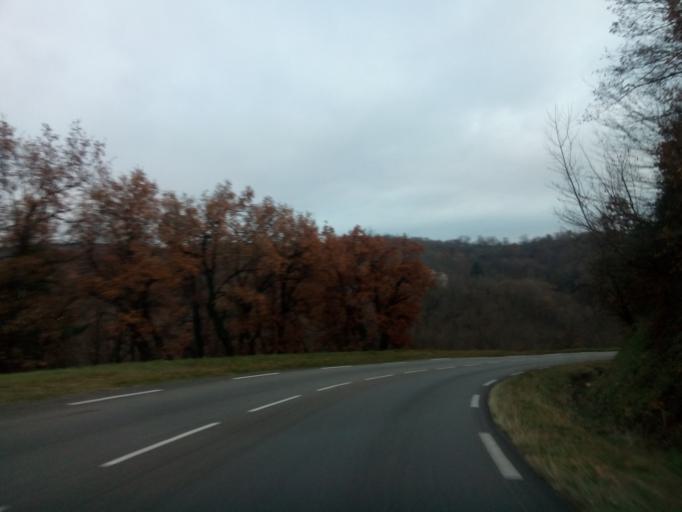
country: FR
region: Rhone-Alpes
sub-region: Departement de la Loire
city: Maclas
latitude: 45.3791
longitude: 4.7128
